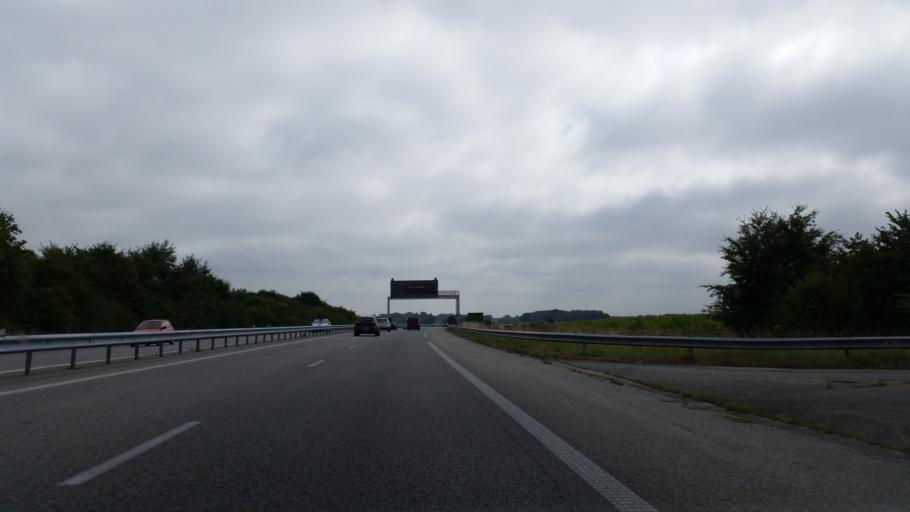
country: FR
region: Haute-Normandie
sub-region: Departement de la Seine-Maritime
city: Sainte-Marie-des-Champs
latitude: 49.6574
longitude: 0.8072
